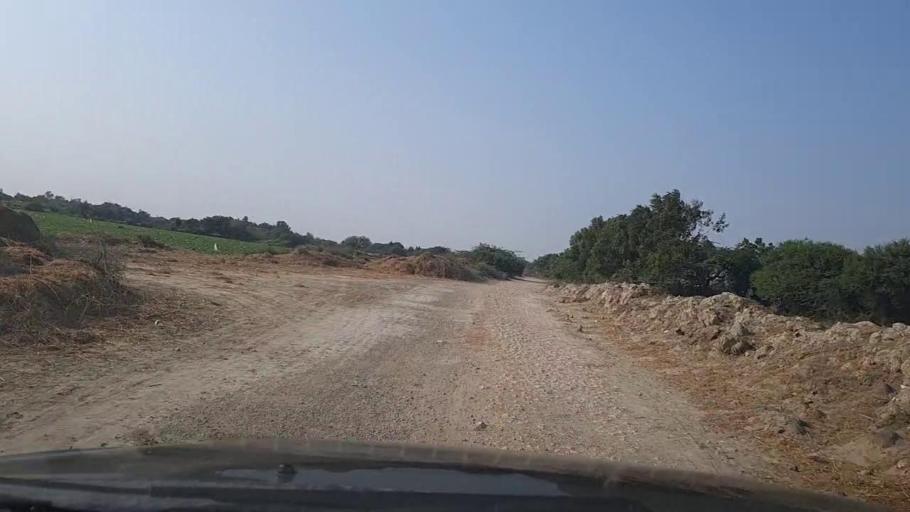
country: PK
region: Sindh
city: Mirpur Sakro
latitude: 24.6366
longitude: 67.7513
